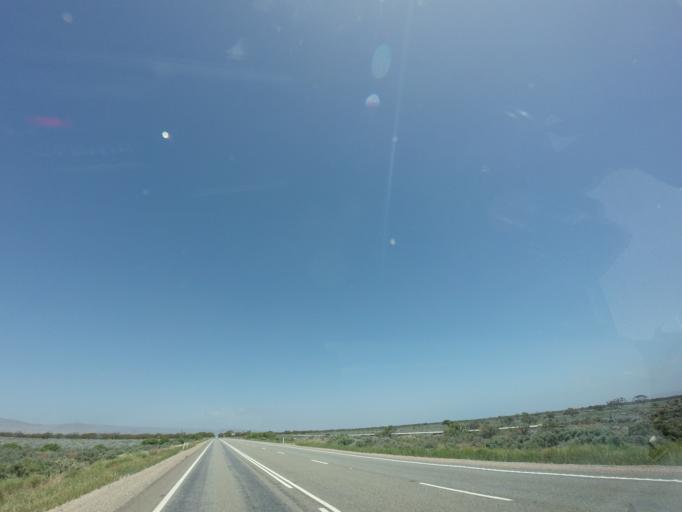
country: AU
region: South Australia
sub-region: Port Augusta
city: Port Augusta
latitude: -32.5828
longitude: 137.8844
